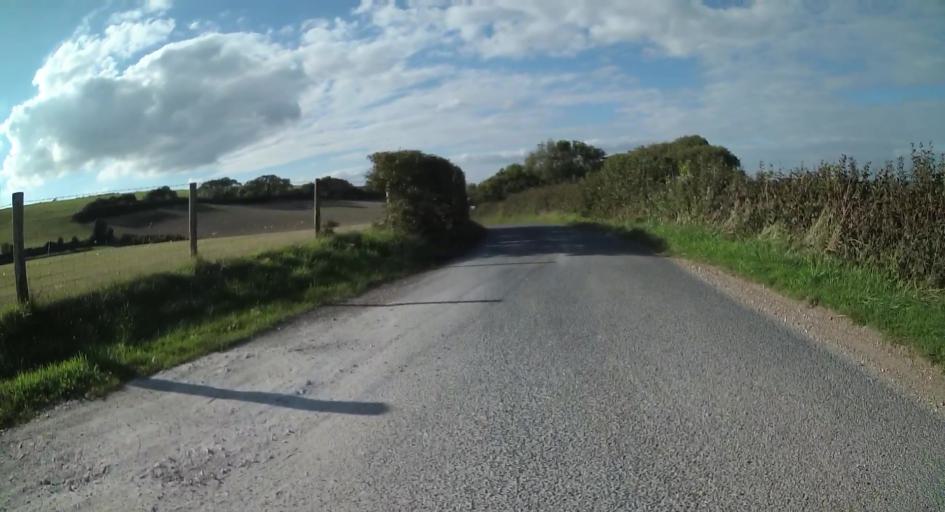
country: GB
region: England
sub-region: Isle of Wight
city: Newport
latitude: 50.6483
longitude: -1.2997
